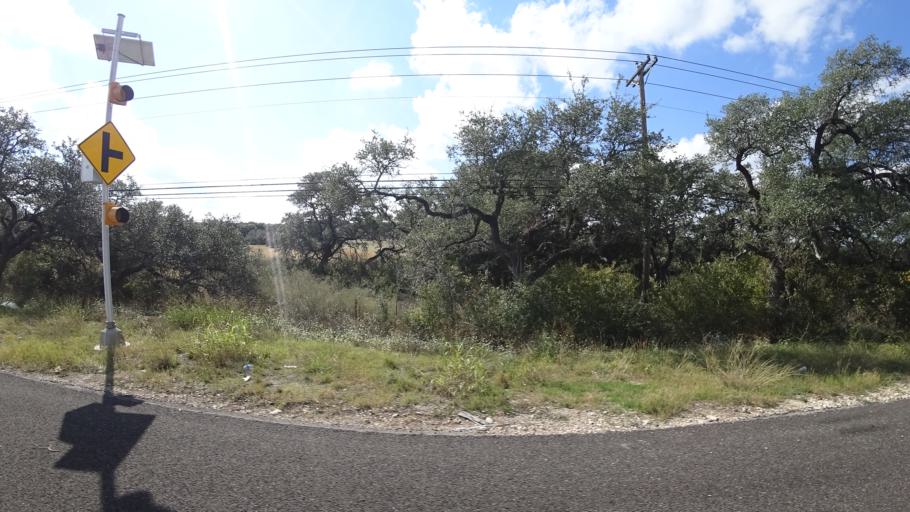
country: US
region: Texas
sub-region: Travis County
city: Barton Creek
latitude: 30.2550
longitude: -97.9023
